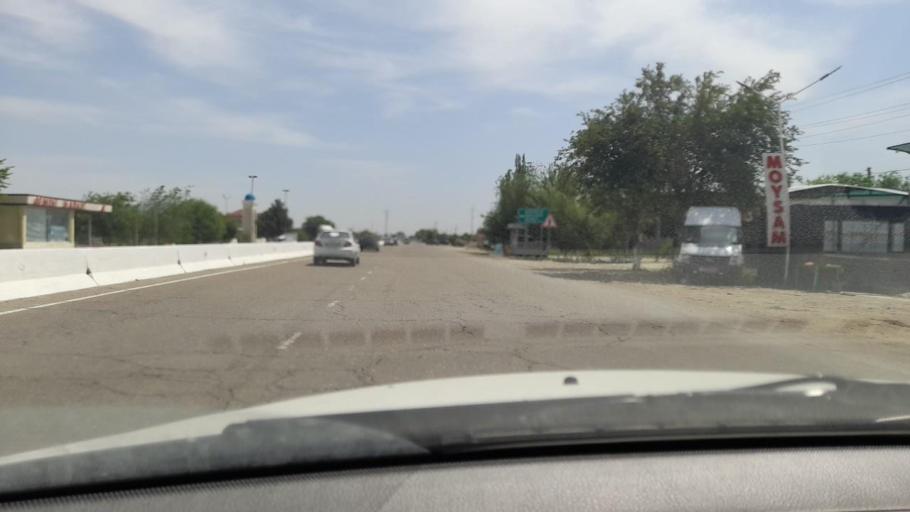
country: UZ
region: Bukhara
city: Ghijduwon
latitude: 40.0886
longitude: 64.6641
